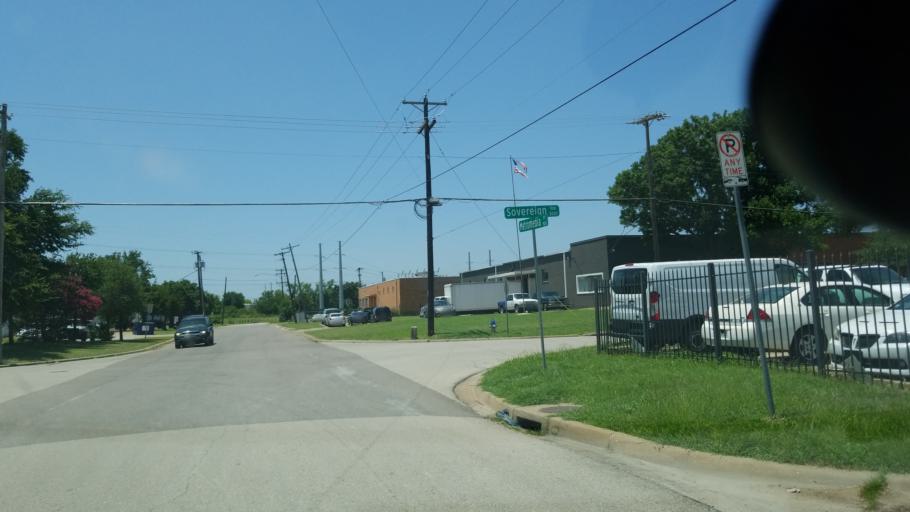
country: US
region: Texas
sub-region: Dallas County
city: Irving
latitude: 32.8156
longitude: -96.8791
